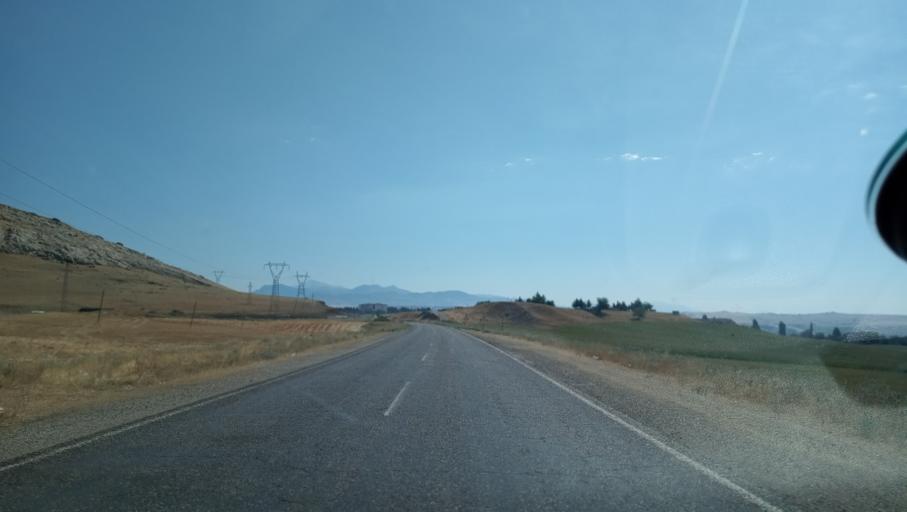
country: TR
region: Diyarbakir
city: Malabadi
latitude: 38.1309
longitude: 41.1829
